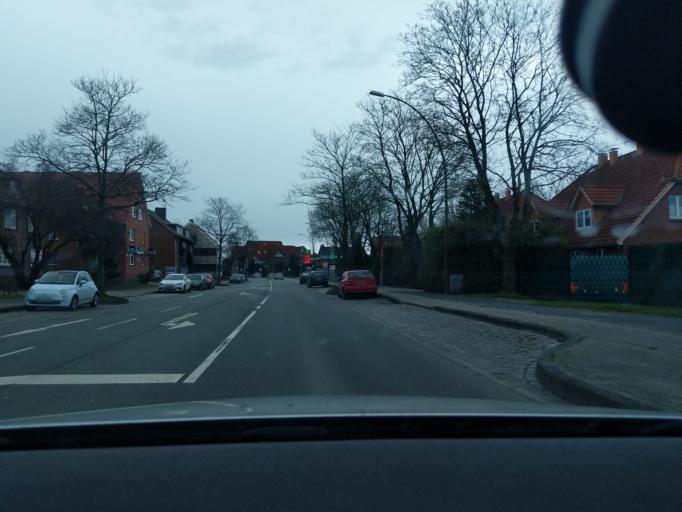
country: DE
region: Lower Saxony
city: Stade
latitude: 53.6016
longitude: 9.4551
